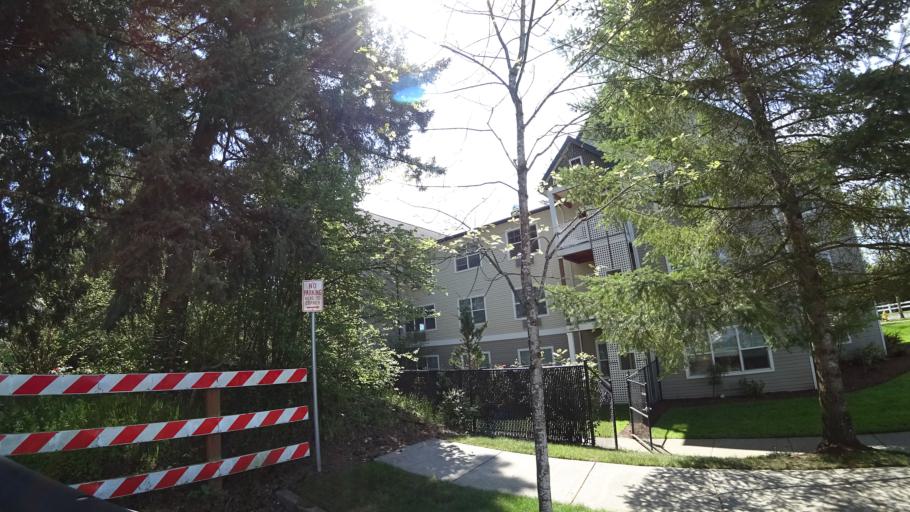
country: US
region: Oregon
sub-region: Washington County
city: Hillsboro
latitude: 45.5054
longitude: -122.9497
